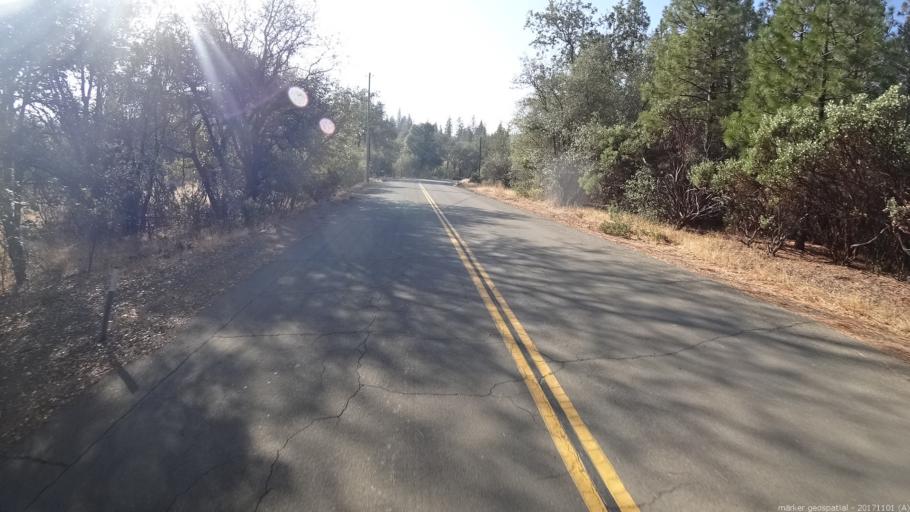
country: US
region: California
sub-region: Shasta County
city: Shasta Lake
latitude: 40.7352
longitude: -122.3165
